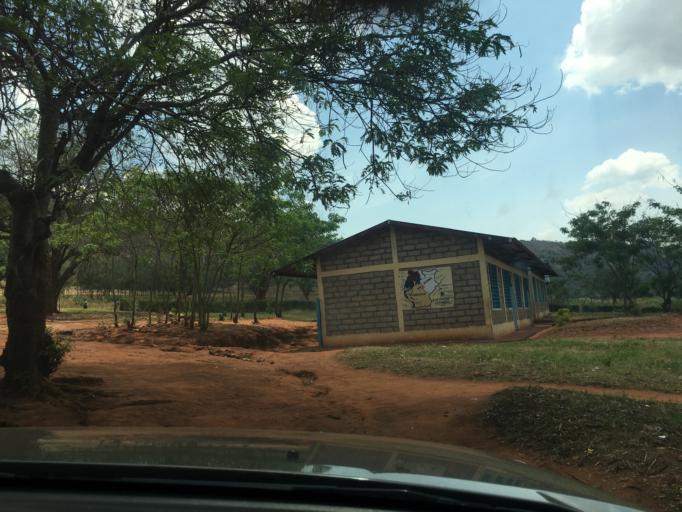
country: RW
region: Eastern Province
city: Kibungo
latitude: -2.1158
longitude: 30.8468
